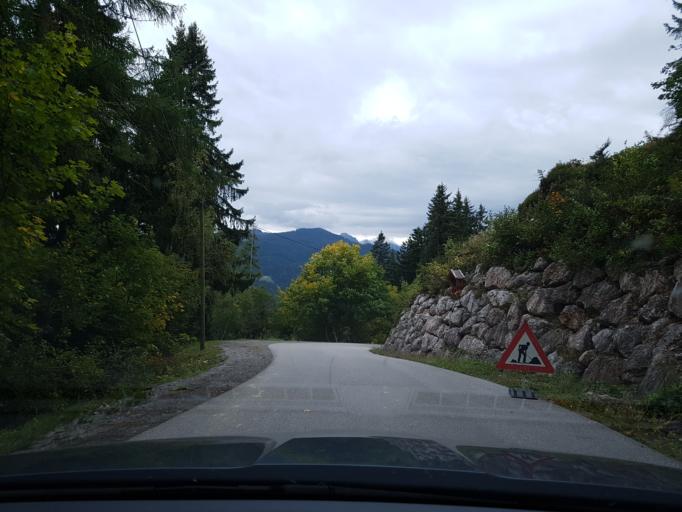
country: AT
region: Salzburg
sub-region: Politischer Bezirk Sankt Johann im Pongau
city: Filzmoos
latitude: 47.4018
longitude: 13.4984
